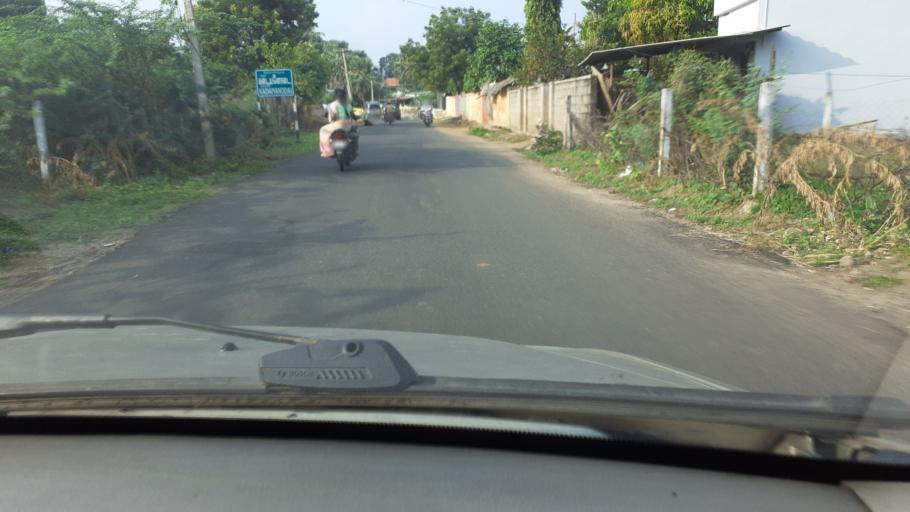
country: IN
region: Tamil Nadu
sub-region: Thoothukkudi
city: Alwar Tirunagari
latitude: 8.5900
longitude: 77.9782
